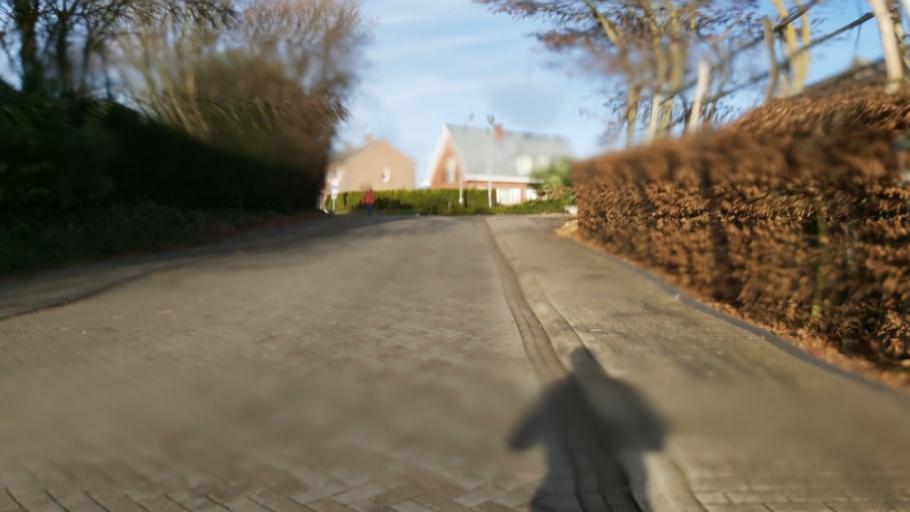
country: BE
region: Flanders
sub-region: Provincie Vlaams-Brabant
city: Hoegaarden
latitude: 50.8190
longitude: 4.8846
